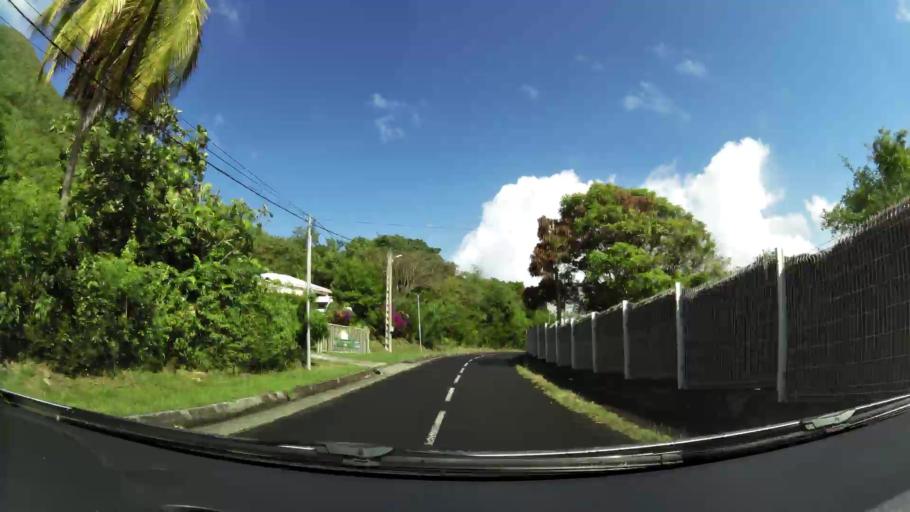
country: MQ
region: Martinique
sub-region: Martinique
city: Les Trois-Ilets
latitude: 14.4628
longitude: -61.0476
